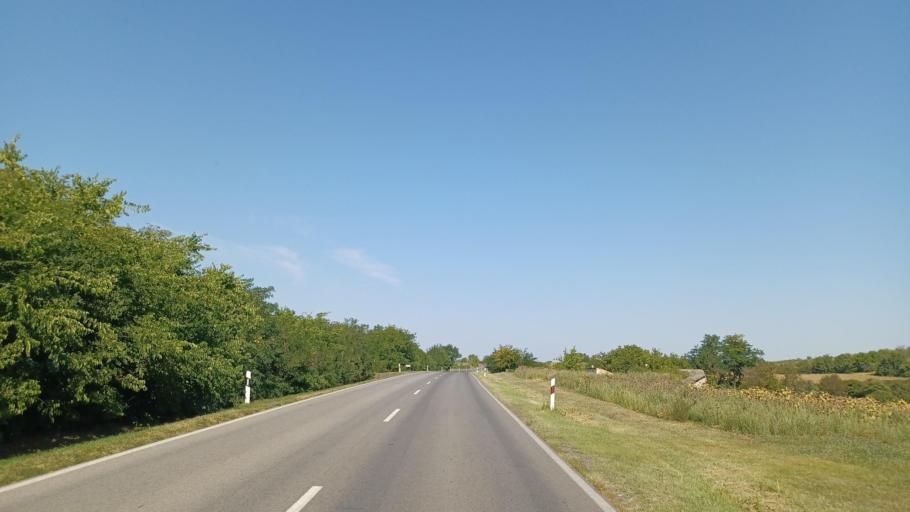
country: HU
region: Tolna
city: Nagydorog
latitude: 46.6385
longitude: 18.6515
